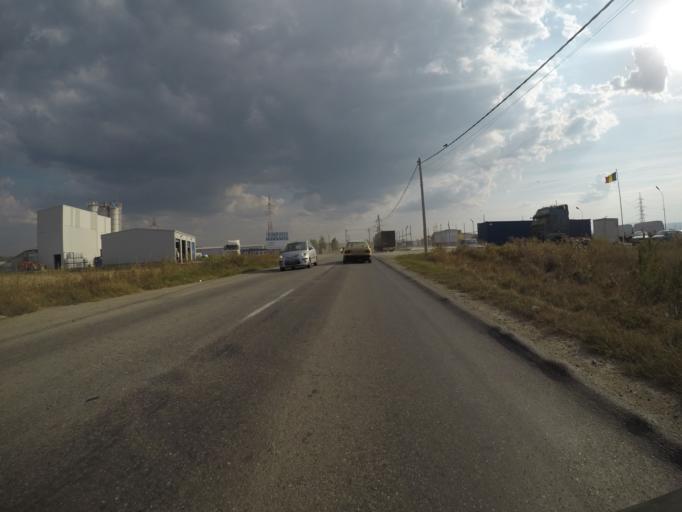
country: RO
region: Cluj
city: Turda
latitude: 46.5421
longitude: 23.7835
